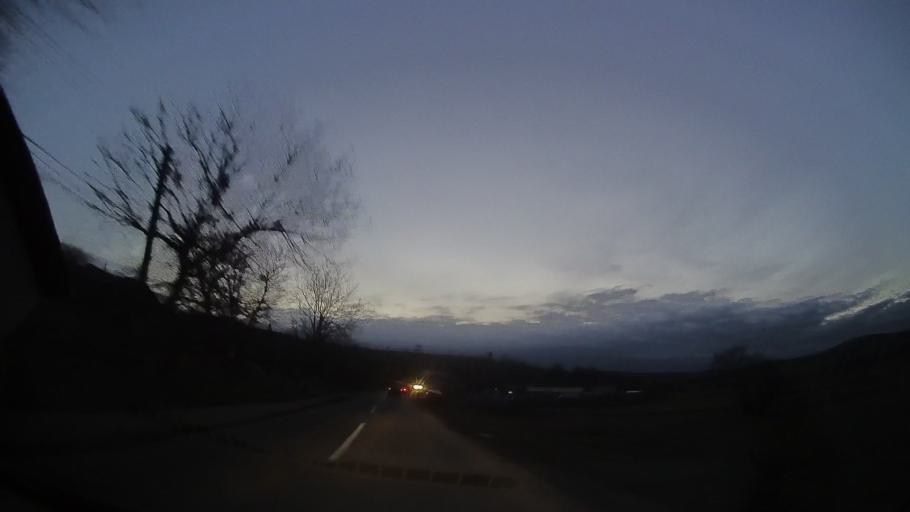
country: RO
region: Mures
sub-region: Comuna Sarmasu
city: Sarmasu
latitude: 46.7594
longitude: 24.1731
